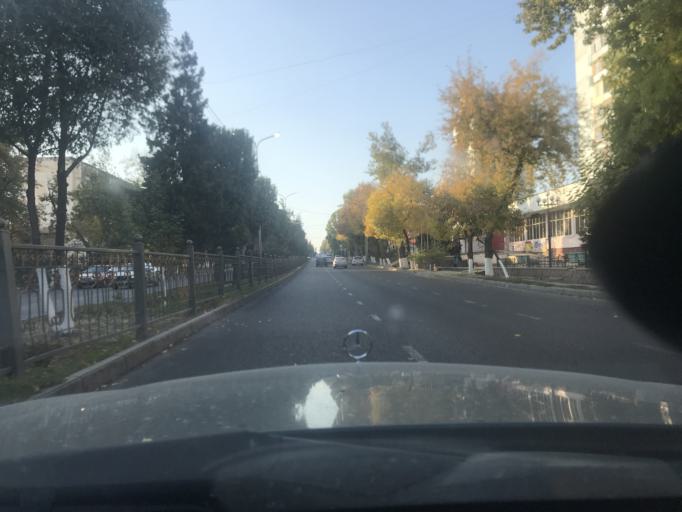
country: KZ
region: Ongtustik Qazaqstan
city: Shymkent
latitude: 42.3004
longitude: 69.6079
